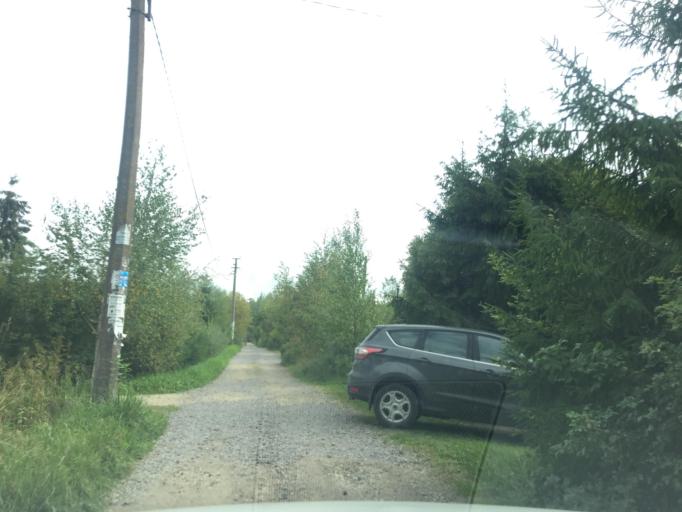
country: RU
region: Leningrad
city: Siverskiy
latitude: 59.2964
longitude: 30.0283
